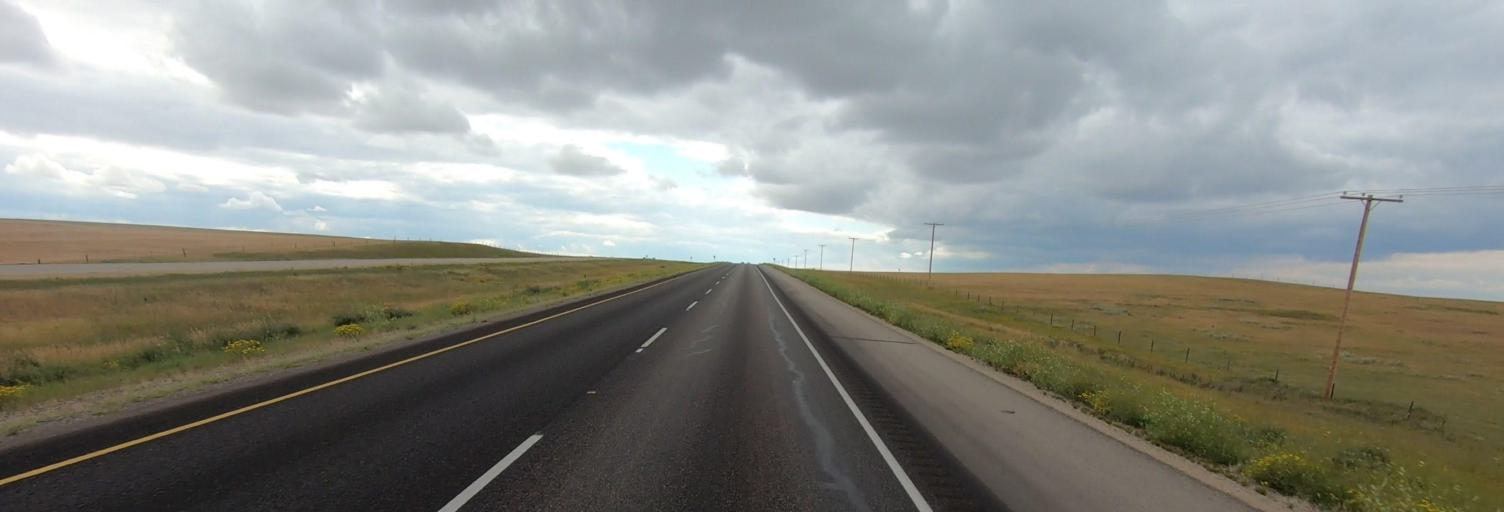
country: CA
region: Saskatchewan
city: Shaunavon
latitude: 50.0707
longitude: -108.6854
